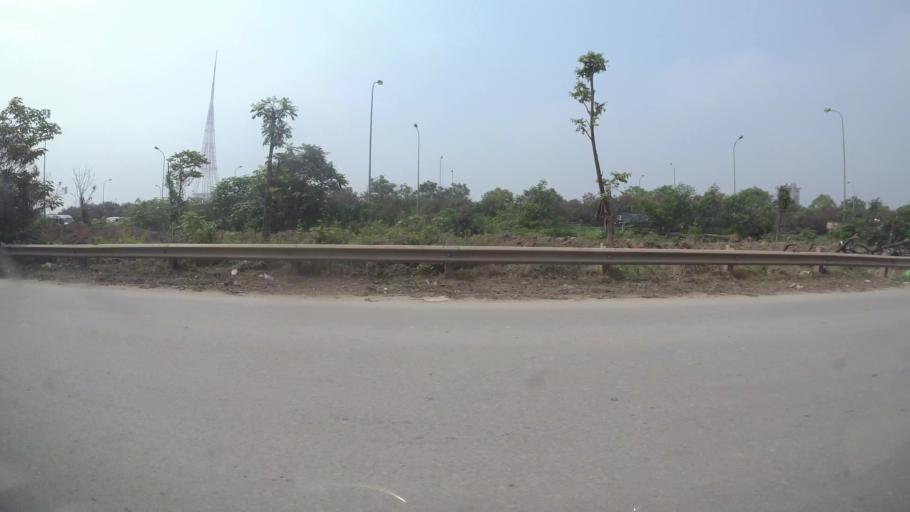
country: VN
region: Ha Noi
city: Cau Dien
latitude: 21.0073
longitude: 105.7610
